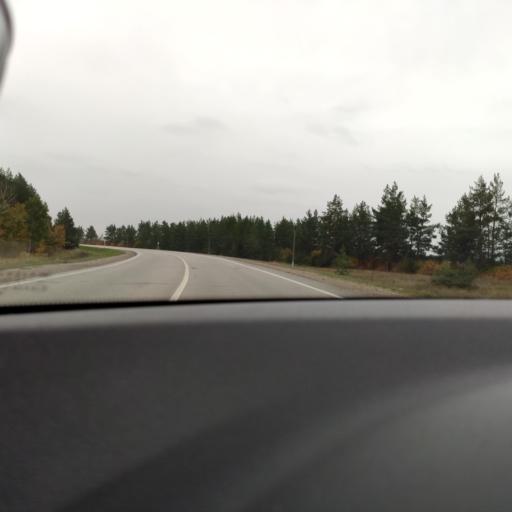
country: RU
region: Samara
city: Mirnyy
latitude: 53.5312
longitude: 50.3047
